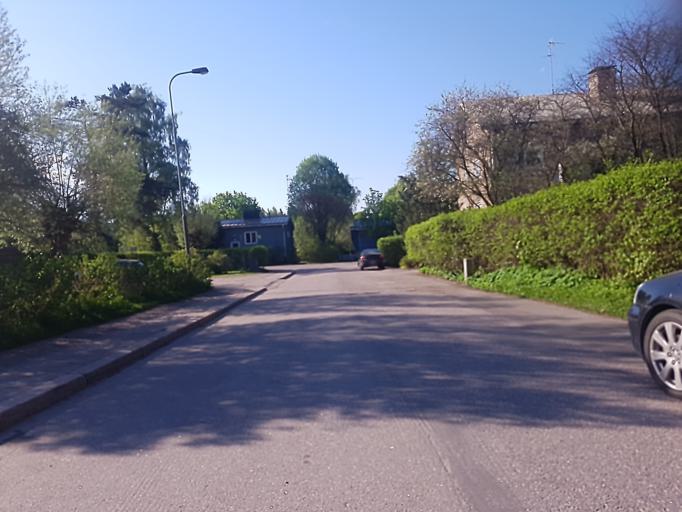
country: FI
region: Uusimaa
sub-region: Helsinki
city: Helsinki
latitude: 60.2359
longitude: 24.9236
